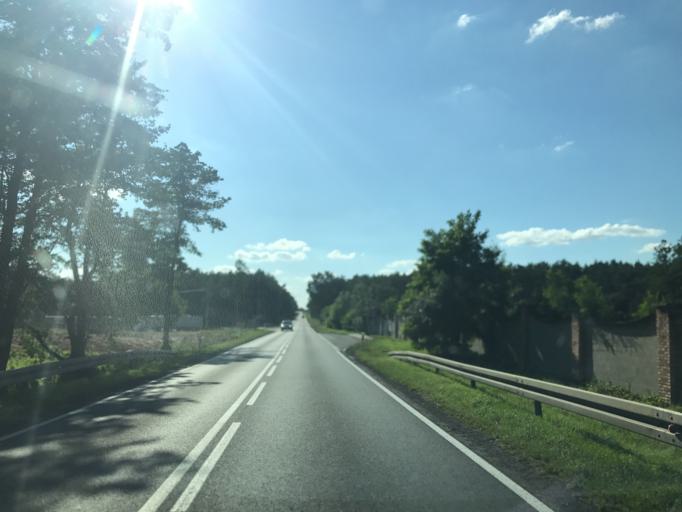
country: PL
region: Kujawsko-Pomorskie
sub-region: Wloclawek
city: Wloclawek
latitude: 52.6248
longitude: 18.9866
